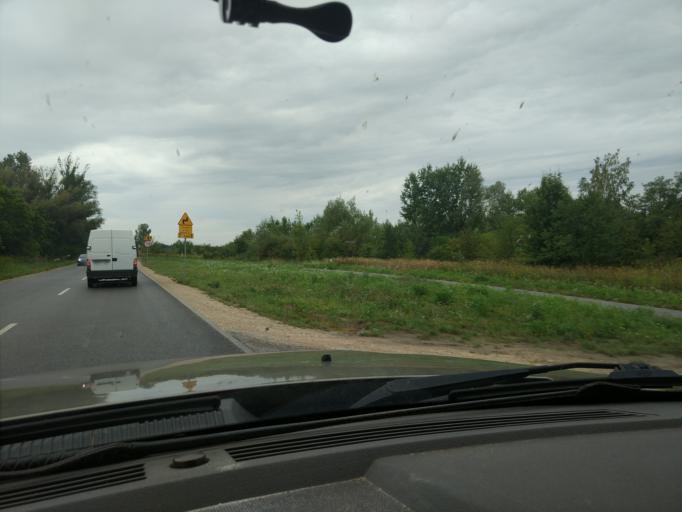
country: PL
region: Masovian Voivodeship
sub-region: Powiat pruszkowski
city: Brwinow
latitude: 52.1744
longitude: 20.7501
